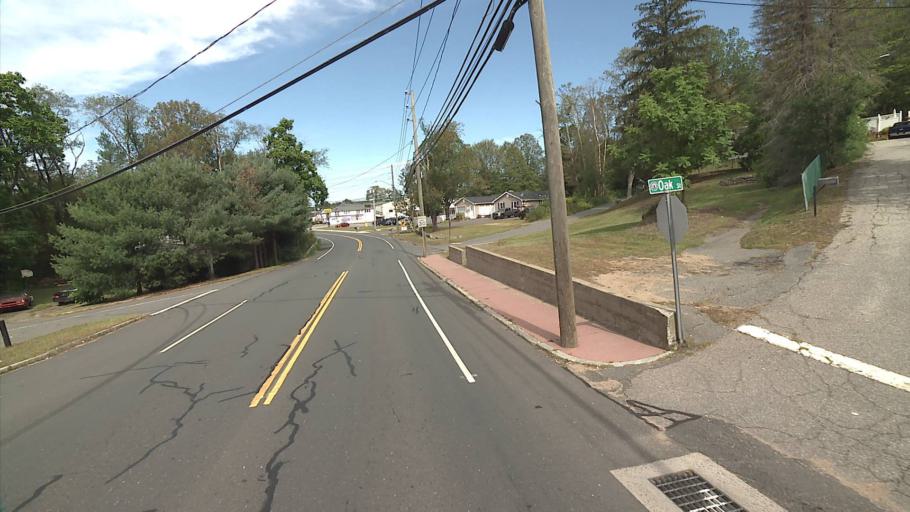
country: US
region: Connecticut
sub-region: Tolland County
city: Stafford Springs
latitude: 41.9590
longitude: -72.3120
